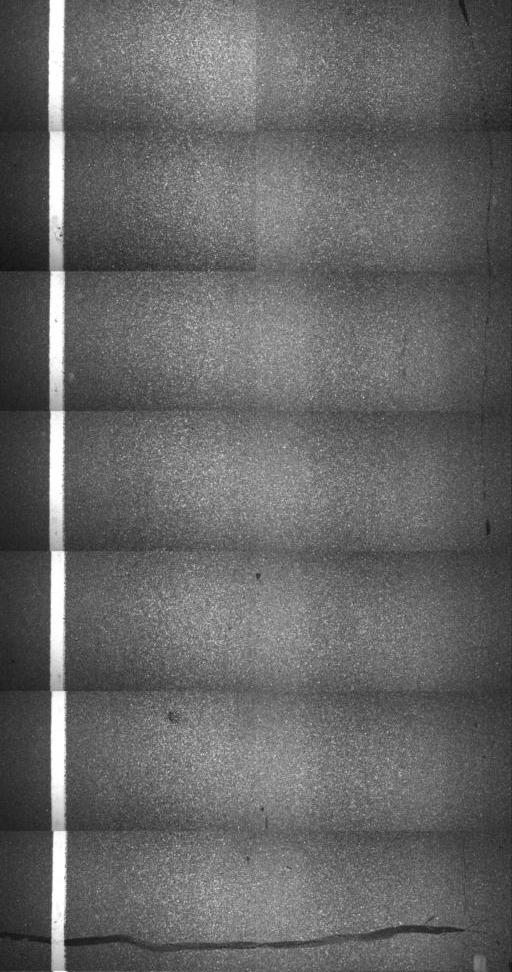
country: US
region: New York
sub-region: Essex County
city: Port Henry
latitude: 44.0758
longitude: -73.3769
